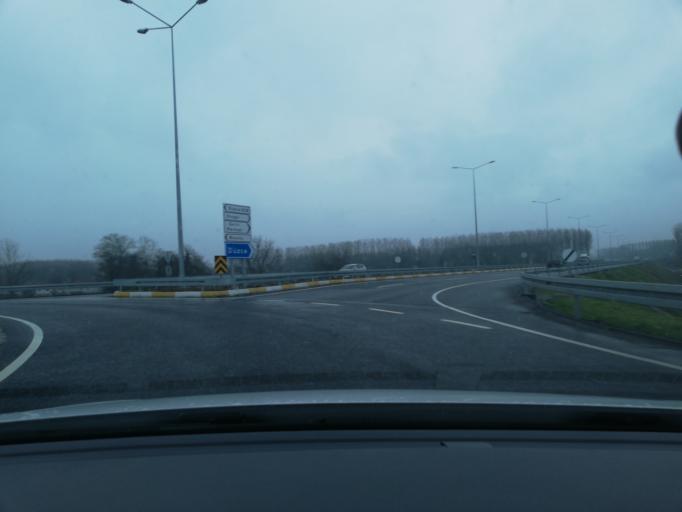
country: TR
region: Duzce
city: Duzce
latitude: 40.8055
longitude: 31.1686
